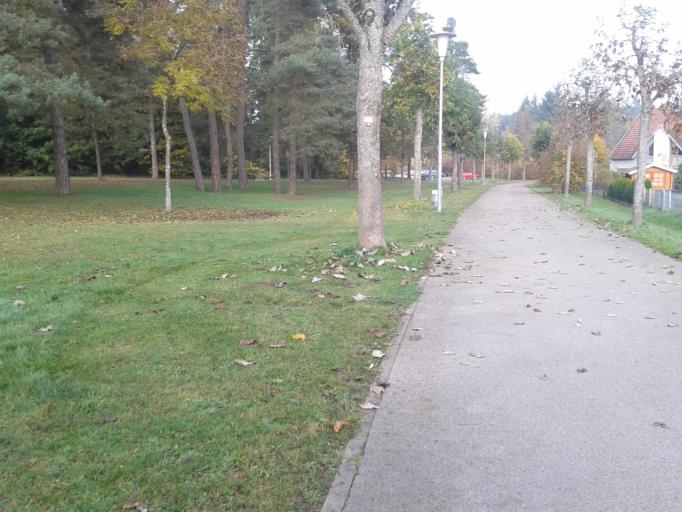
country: DE
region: Bavaria
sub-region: Regierungsbezirk Mittelfranken
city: Pleinfeld
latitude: 49.1088
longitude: 10.9750
